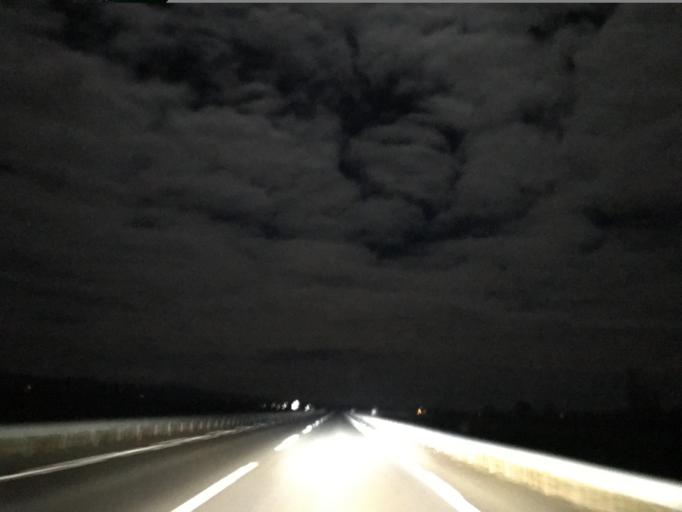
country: FR
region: Auvergne
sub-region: Departement de l'Allier
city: Saint-Yorre
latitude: 46.0620
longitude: 3.4467
